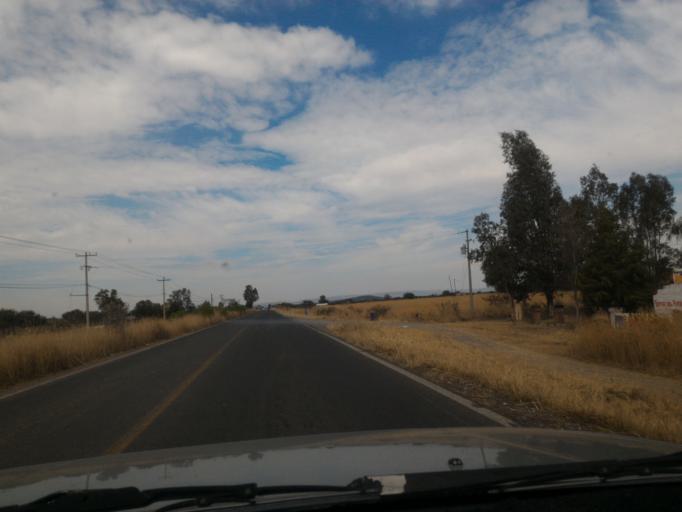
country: MX
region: Guanajuato
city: Ciudad Manuel Doblado
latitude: 20.7577
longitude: -101.9660
